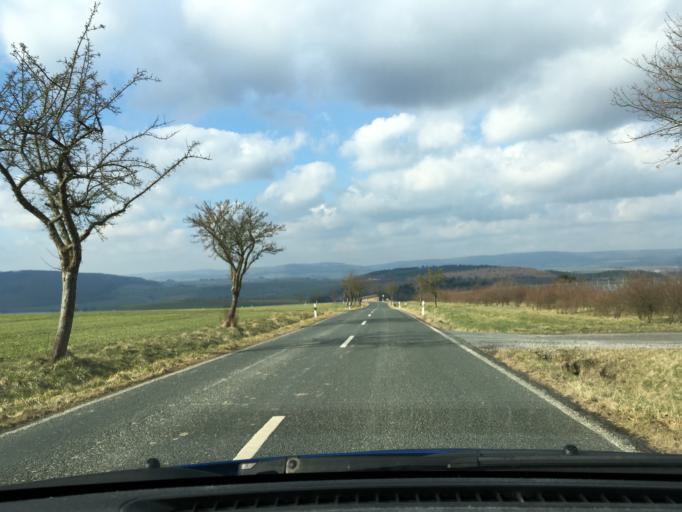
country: DE
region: Lower Saxony
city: Uslar
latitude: 51.6053
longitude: 9.6383
